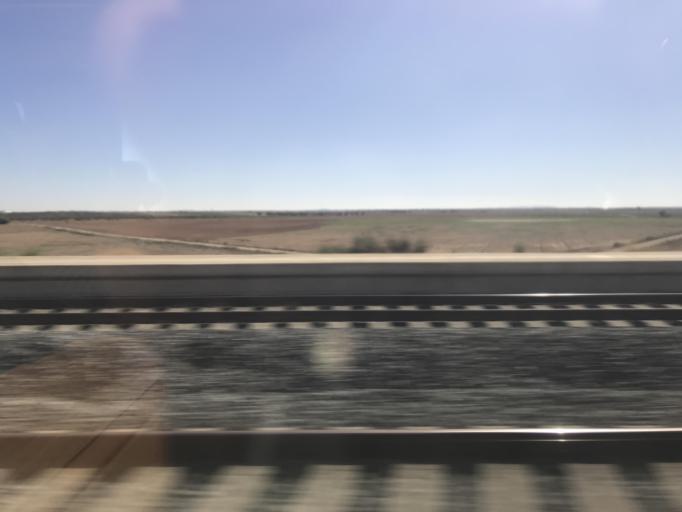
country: ES
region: Castille-La Mancha
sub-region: Province of Toledo
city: Villarrubia de Santiago
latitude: 39.9531
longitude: -3.3787
